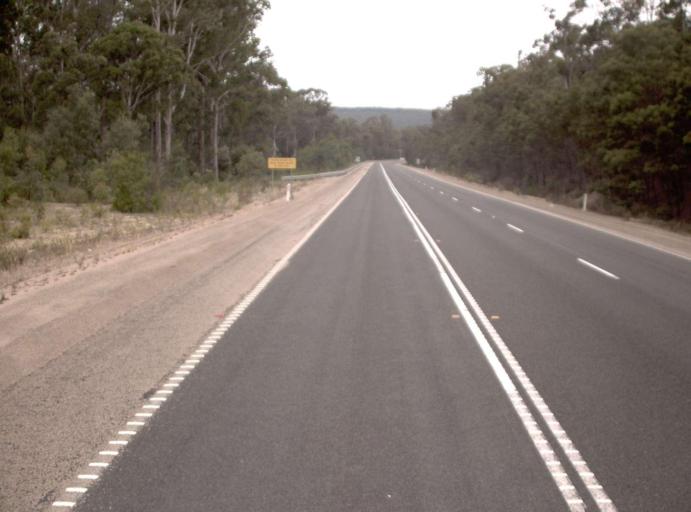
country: AU
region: Victoria
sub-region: East Gippsland
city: Lakes Entrance
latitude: -37.7206
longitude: 148.0808
